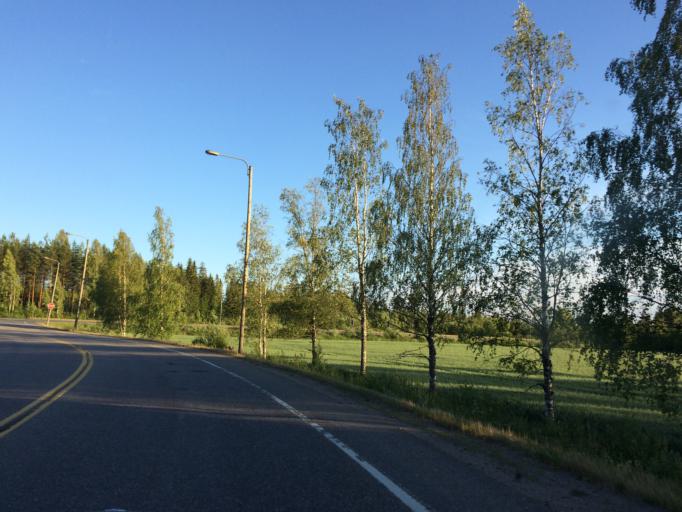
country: FI
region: Haeme
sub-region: Riihimaeki
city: Riihimaeki
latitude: 60.7503
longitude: 24.7213
